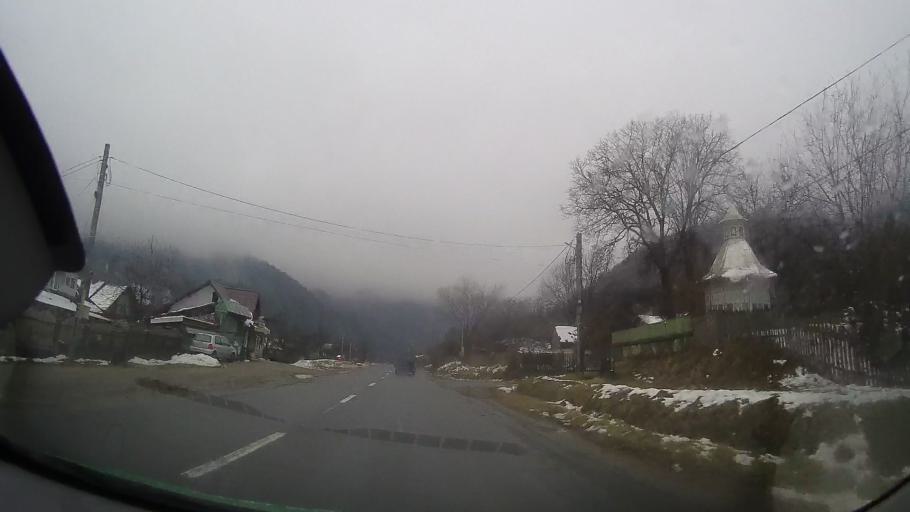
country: RO
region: Neamt
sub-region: Comuna Pangarati
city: Stejaru
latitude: 46.8967
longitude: 26.1706
